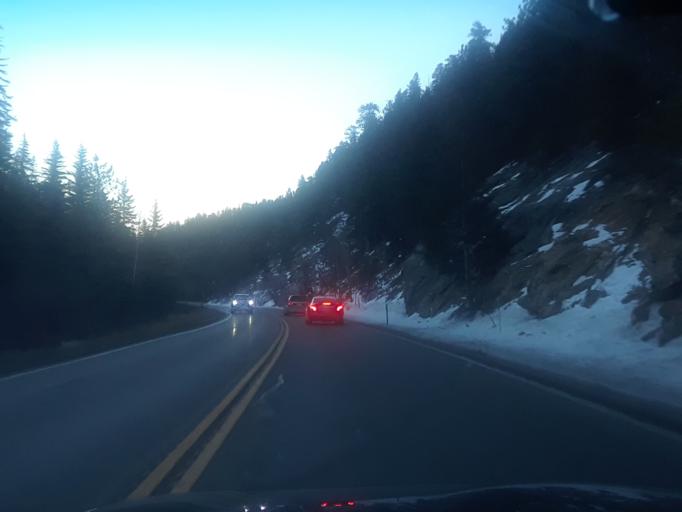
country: US
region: Colorado
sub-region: Clear Creek County
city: Georgetown
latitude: 39.4461
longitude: -105.6141
